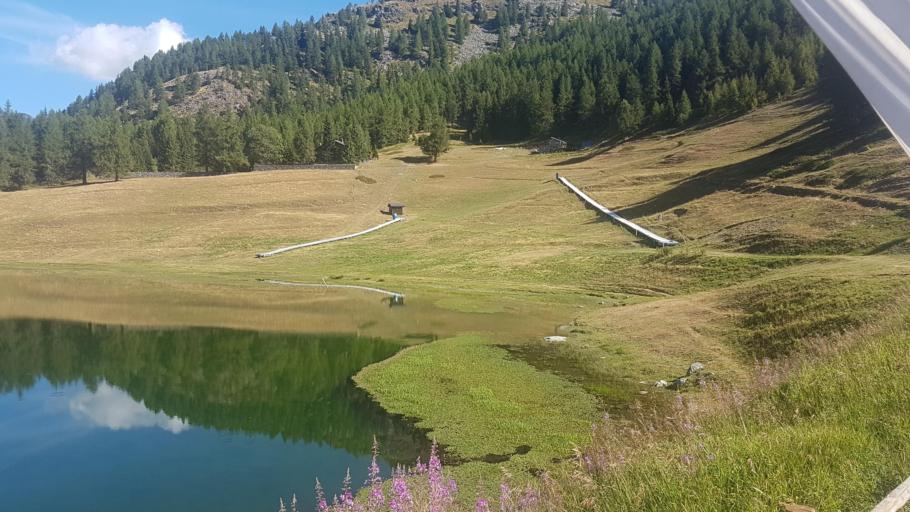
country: IT
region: Aosta Valley
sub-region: Valle d'Aosta
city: Chamois
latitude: 45.8449
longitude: 7.6239
